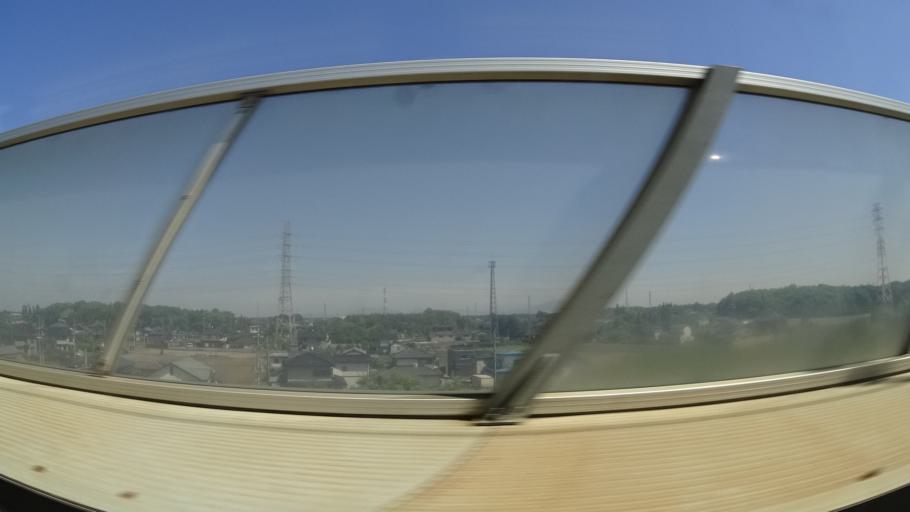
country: JP
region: Tochigi
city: Mibu
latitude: 36.3668
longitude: 139.8377
